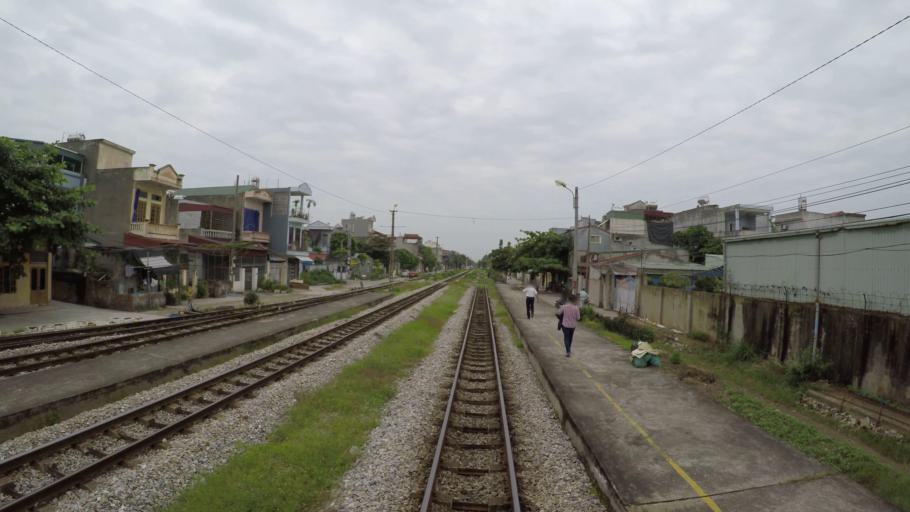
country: VN
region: Hai Duong
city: Thanh Pho Hai Duong
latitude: 20.9444
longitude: 106.3109
